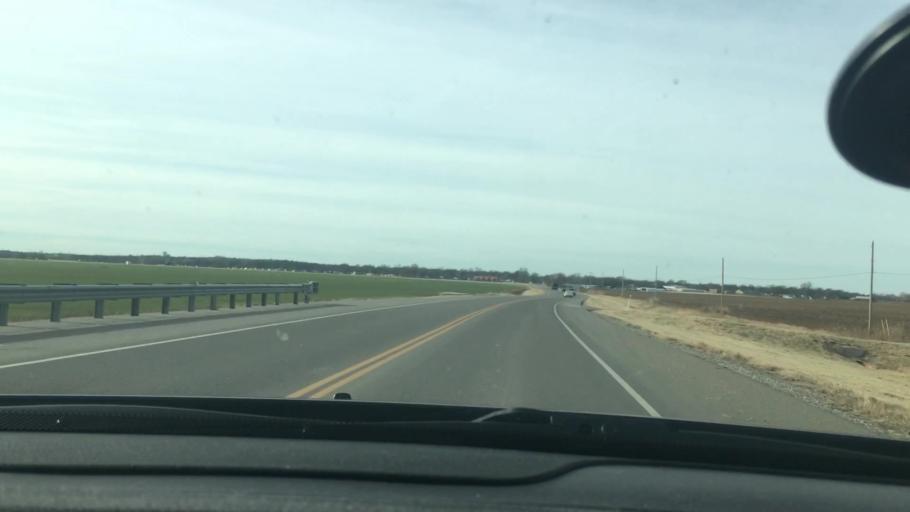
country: US
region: Oklahoma
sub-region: Garvin County
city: Pauls Valley
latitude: 34.7595
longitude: -97.1987
